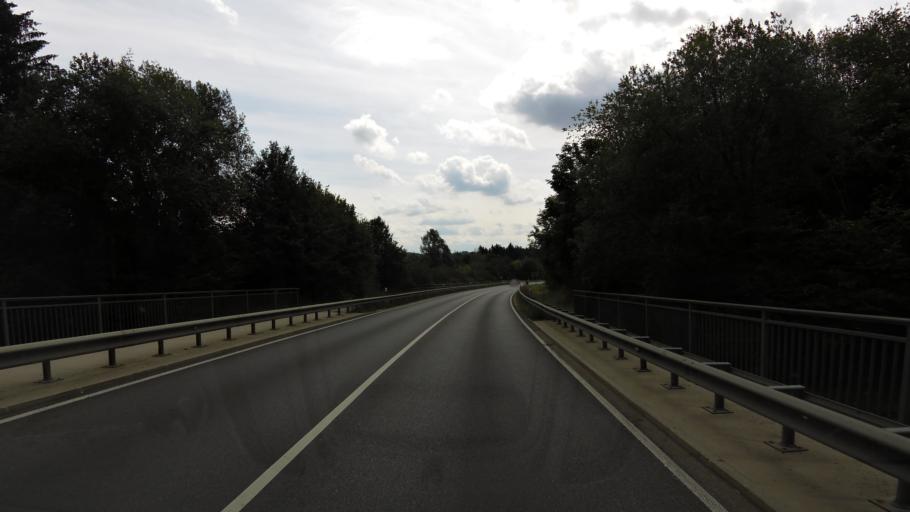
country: DE
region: Bavaria
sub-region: Upper Bavaria
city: Unterneukirchen
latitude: 48.1539
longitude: 12.6128
